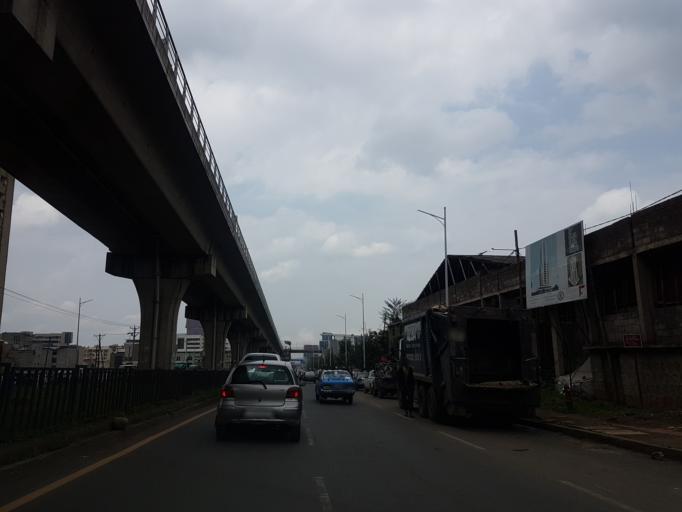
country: ET
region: Adis Abeba
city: Addis Ababa
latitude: 9.0176
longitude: 38.7349
